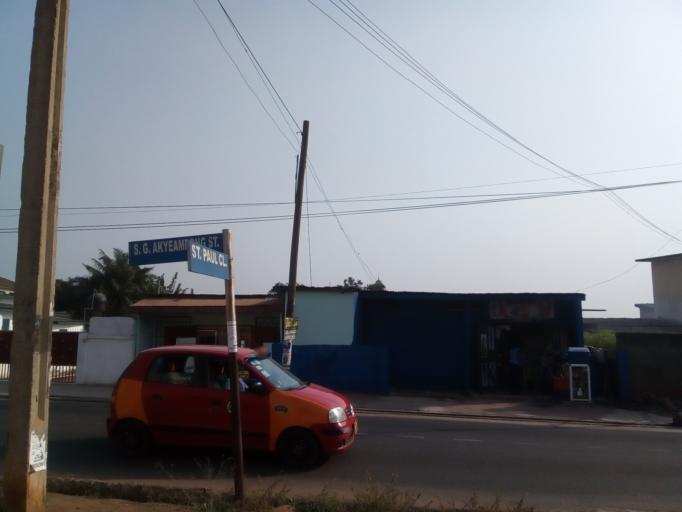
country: GH
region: Greater Accra
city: Accra
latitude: 5.5853
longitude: -0.2143
